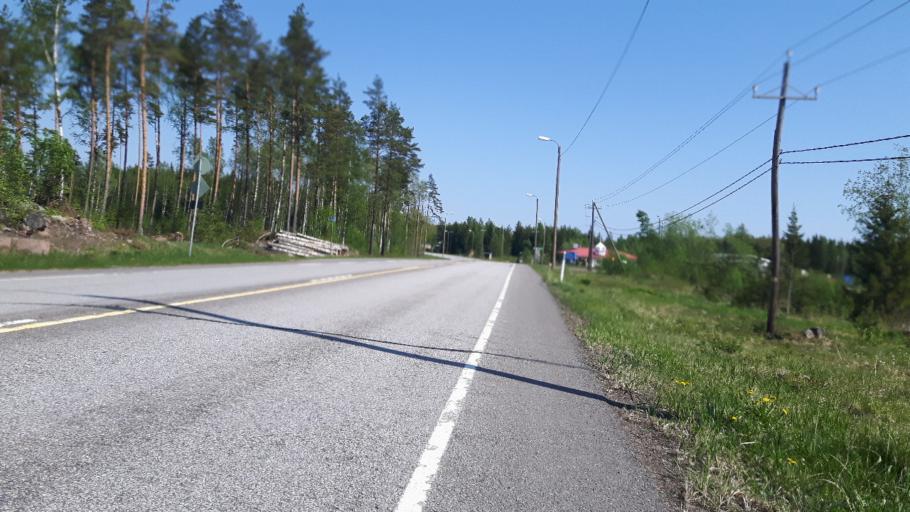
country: FI
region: Kymenlaakso
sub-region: Kotka-Hamina
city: Broby
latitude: 60.4887
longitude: 26.6620
